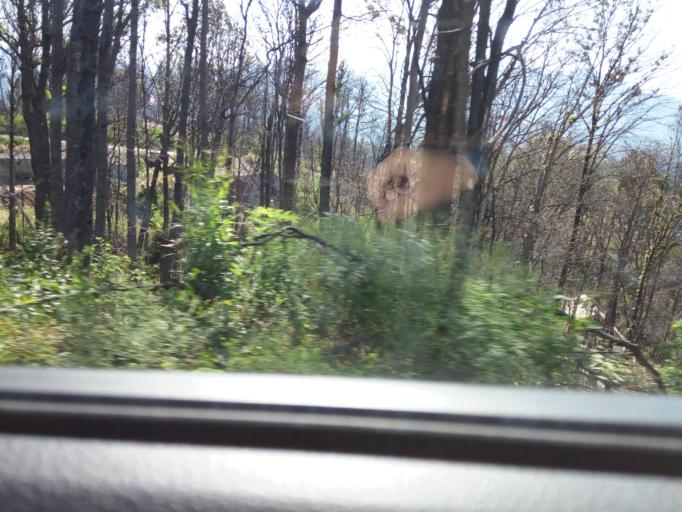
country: US
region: Tennessee
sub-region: Sevier County
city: Gatlinburg
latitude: 35.7223
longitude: -83.5290
